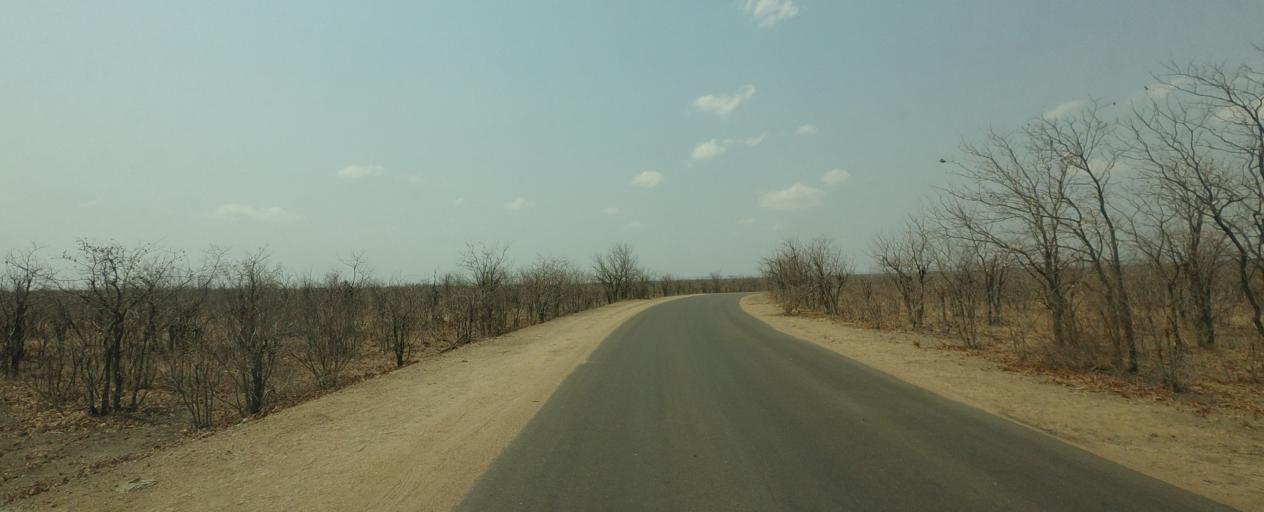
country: ZA
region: Limpopo
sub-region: Mopani District Municipality
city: Phalaborwa
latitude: -23.5192
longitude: 31.4029
